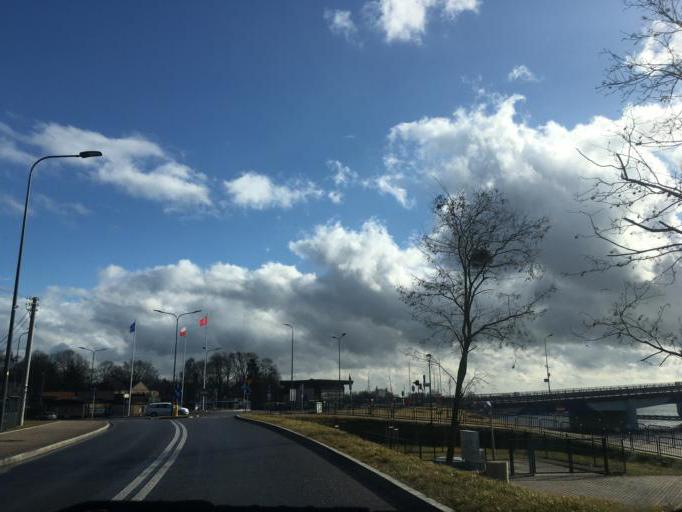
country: PL
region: Pomeranian Voivodeship
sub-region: Powiat gdanski
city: Cedry Wielkie
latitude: 54.3441
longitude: 18.8245
